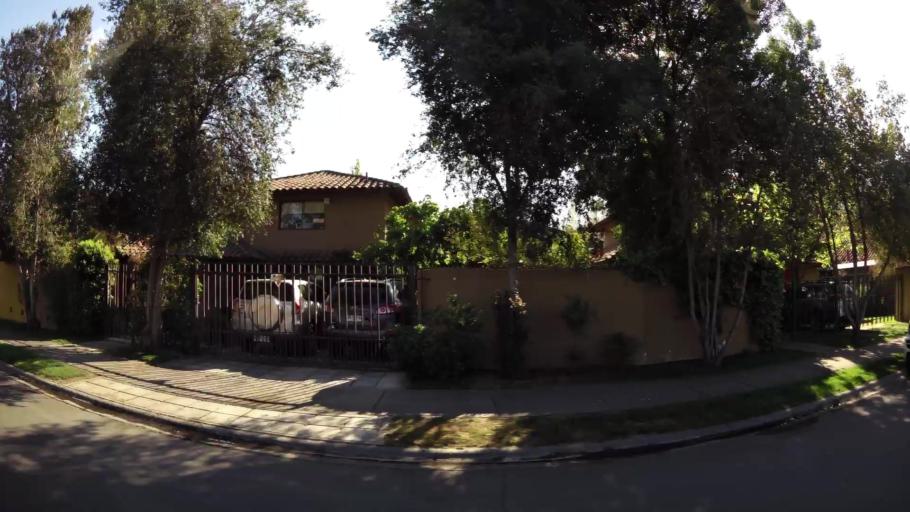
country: CL
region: Santiago Metropolitan
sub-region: Provincia de Chacabuco
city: Chicureo Abajo
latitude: -33.3493
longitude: -70.6659
